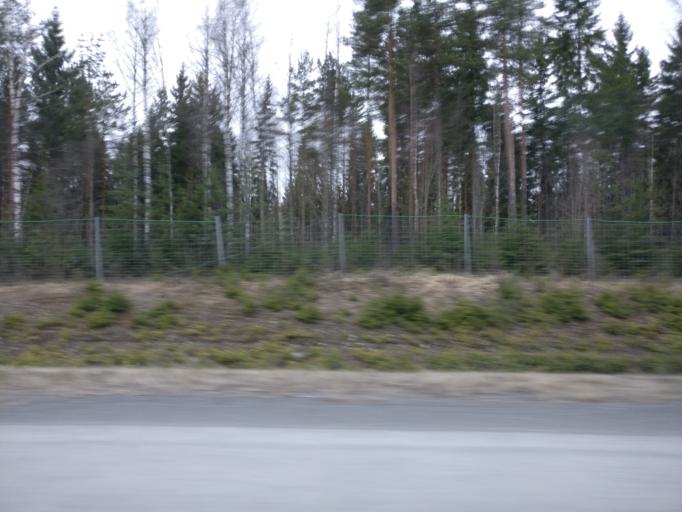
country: FI
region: Pirkanmaa
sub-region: Tampere
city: Lempaeaelae
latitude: 61.2751
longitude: 23.8124
